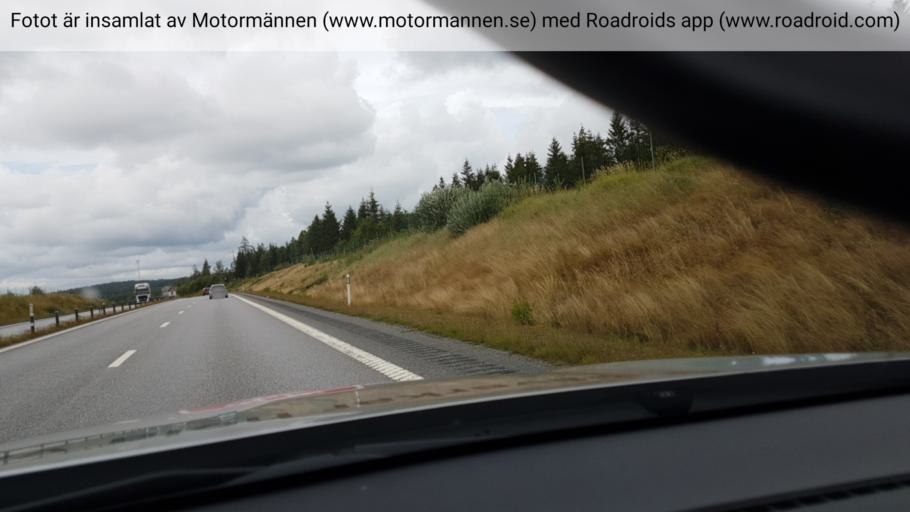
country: SE
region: Vaestra Goetaland
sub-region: Tanums Kommun
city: Tanumshede
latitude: 58.6242
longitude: 11.4478
